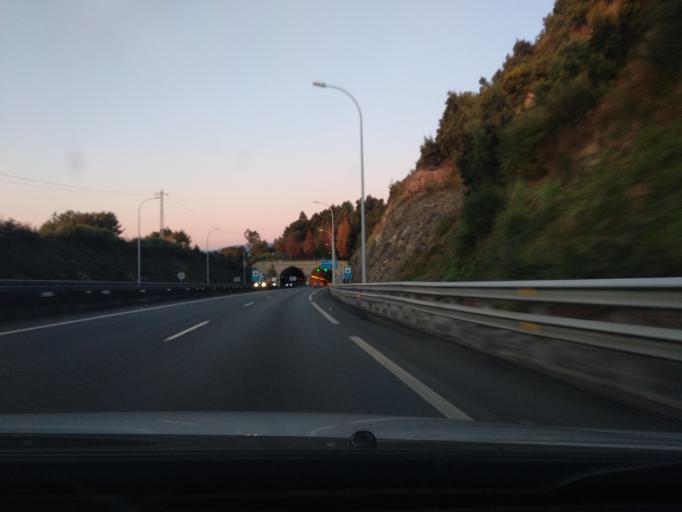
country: ES
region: Galicia
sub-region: Provincia de Pontevedra
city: Vigo
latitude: 42.2487
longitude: -8.6817
